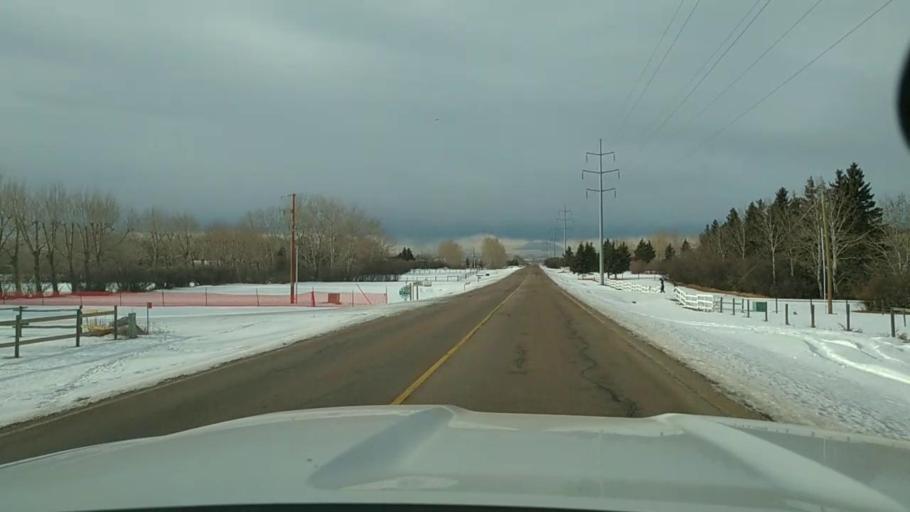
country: CA
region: Alberta
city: Airdrie
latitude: 51.2417
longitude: -113.9748
